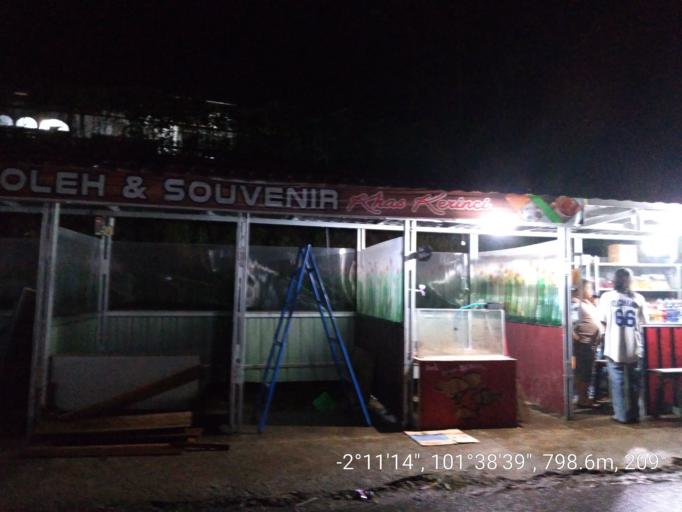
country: ID
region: Jambi
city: Sungai Penuh
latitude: -2.1873
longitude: 101.6444
